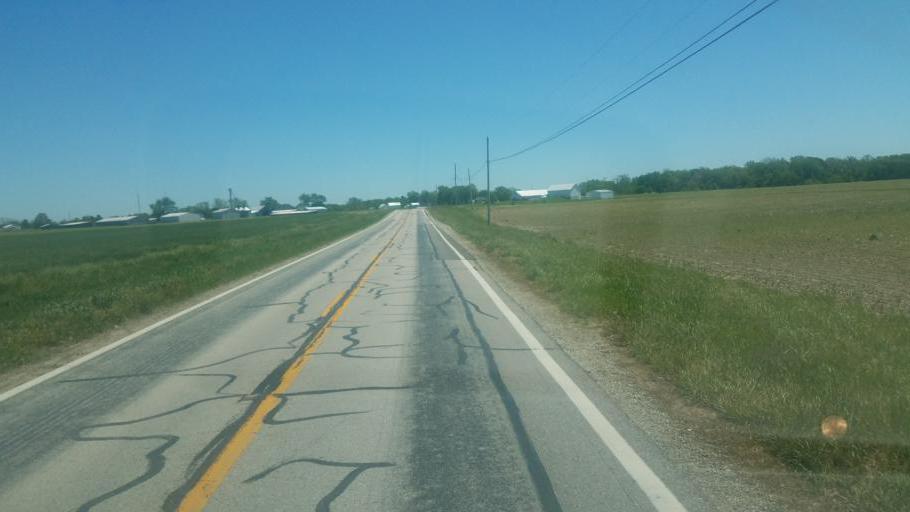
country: US
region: Ohio
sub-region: Darke County
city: Versailles
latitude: 40.2384
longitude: -84.5102
